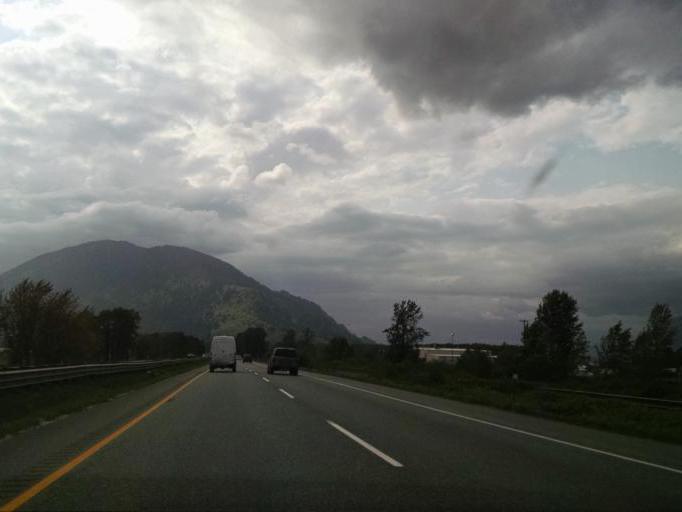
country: CA
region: British Columbia
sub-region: Fraser Valley Regional District
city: Chilliwack
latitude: 49.1394
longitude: -122.0532
